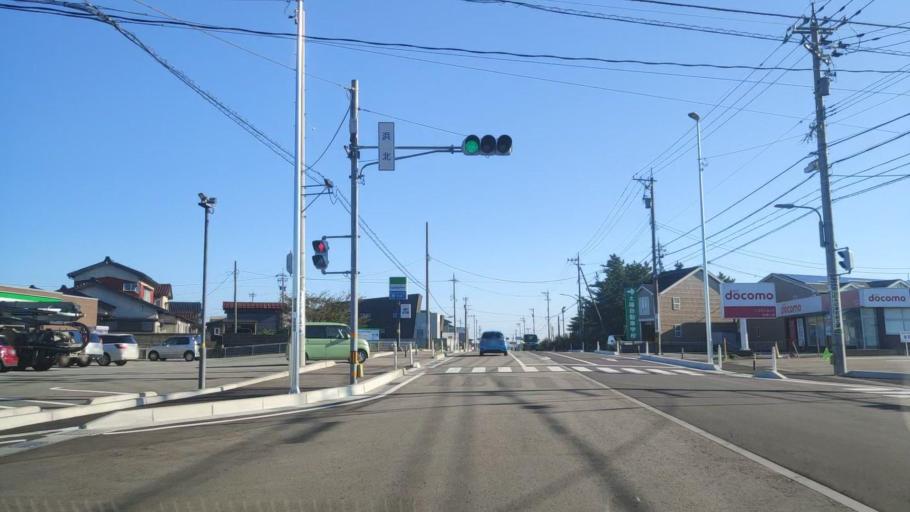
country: JP
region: Ishikawa
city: Tsubata
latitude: 36.7330
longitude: 136.7003
